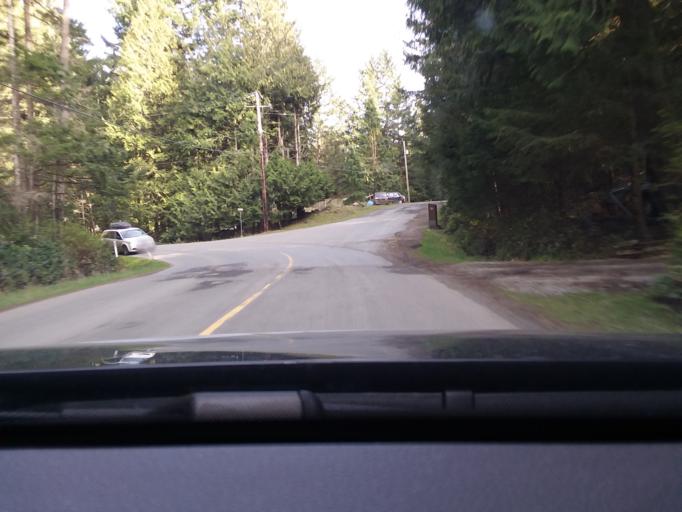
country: CA
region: British Columbia
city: North Saanich
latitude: 48.7714
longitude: -123.2922
